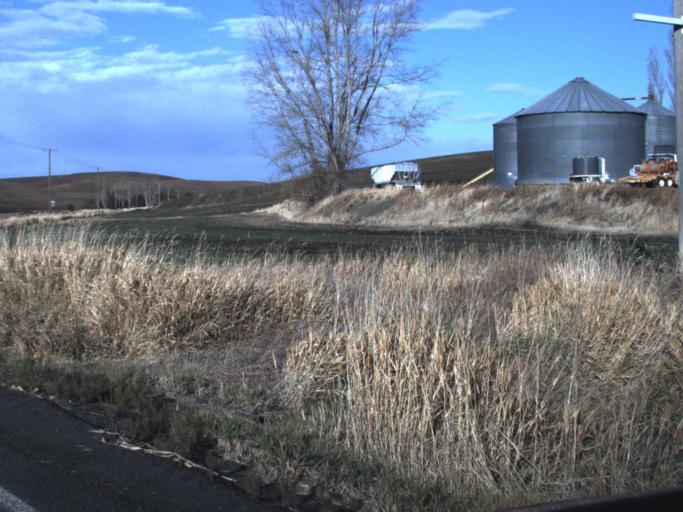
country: US
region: Washington
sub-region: Whitman County
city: Pullman
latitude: 46.7082
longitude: -117.2686
